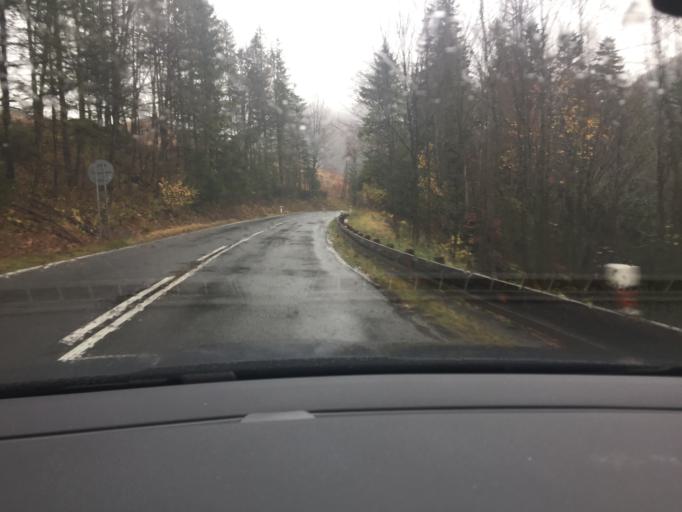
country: SK
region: Presovsky
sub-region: Okres Poprad
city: Zdiar
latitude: 49.2434
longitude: 20.3094
